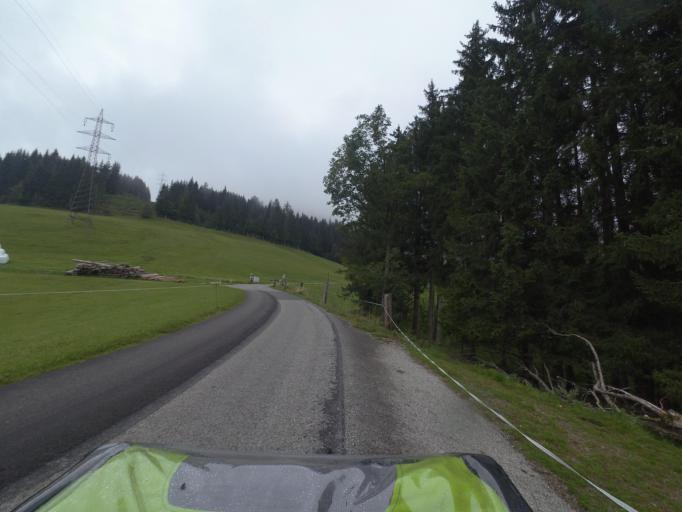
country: AT
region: Salzburg
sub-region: Politischer Bezirk Sankt Johann im Pongau
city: Sankt Johann im Pongau
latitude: 47.3602
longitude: 13.1714
